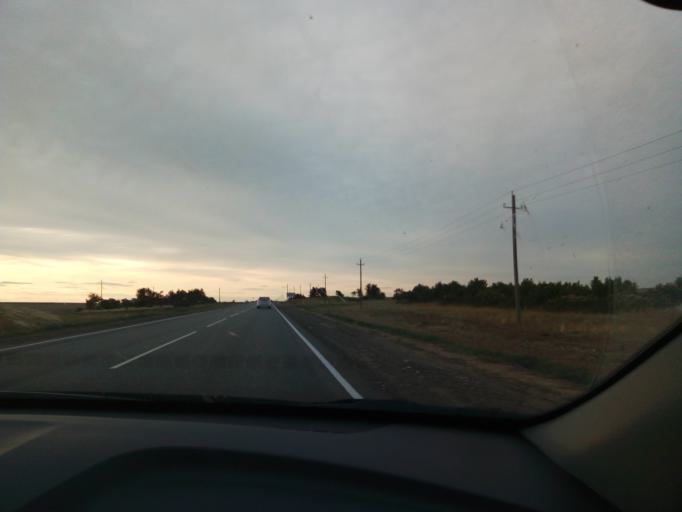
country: RU
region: Volgograd
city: Primorsk
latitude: 49.2493
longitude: 44.8896
